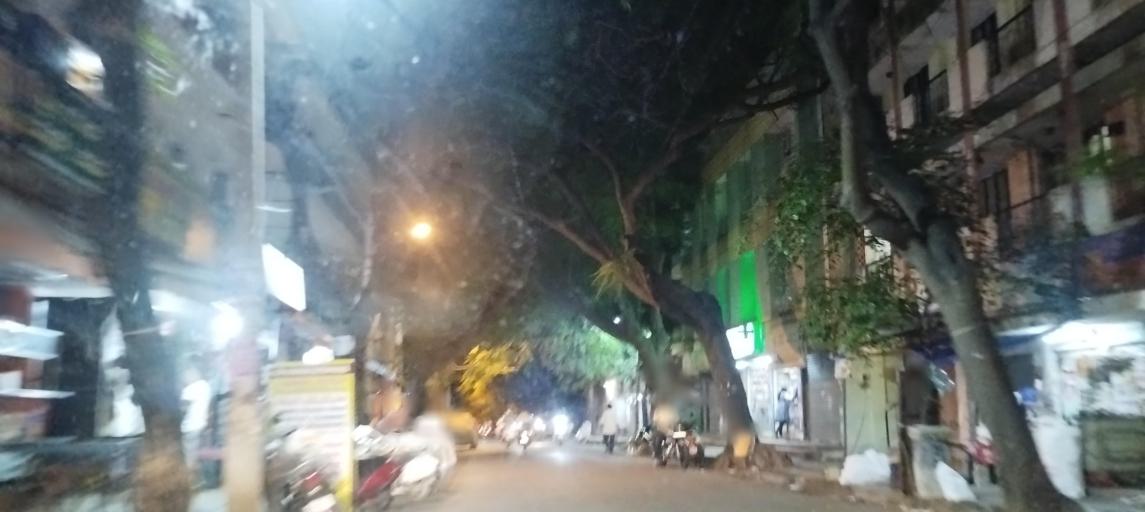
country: IN
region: Karnataka
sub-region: Bangalore Urban
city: Bangalore
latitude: 12.9397
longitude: 77.5552
